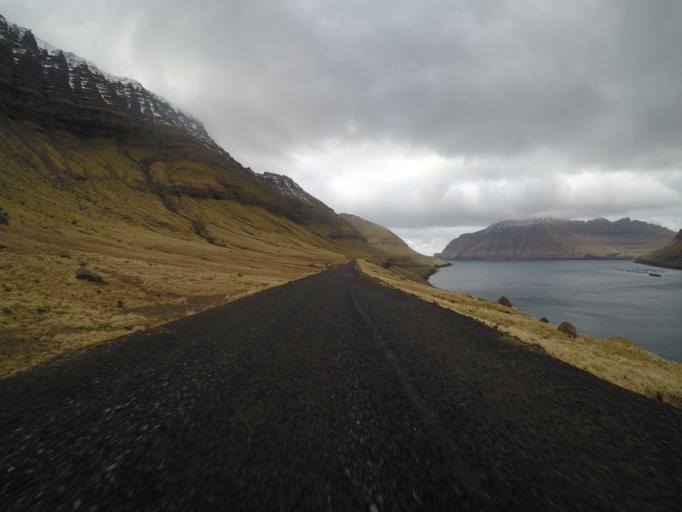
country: FO
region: Nordoyar
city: Klaksvik
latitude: 62.3315
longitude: -6.5742
